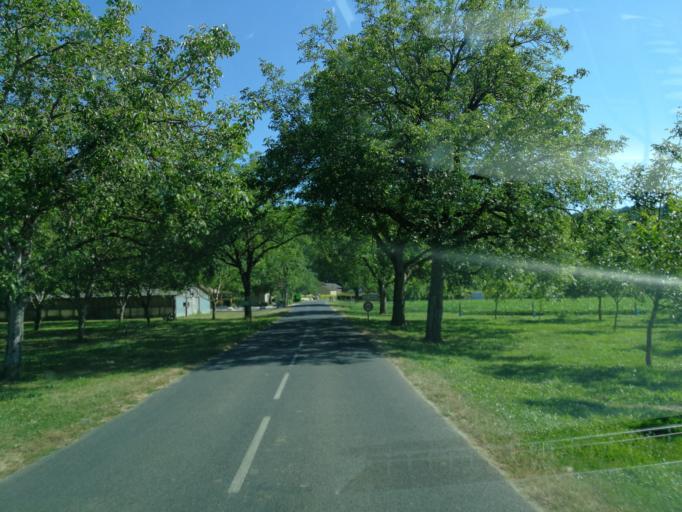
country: FR
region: Midi-Pyrenees
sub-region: Departement du Lot
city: Souillac
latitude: 44.8710
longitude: 1.4420
